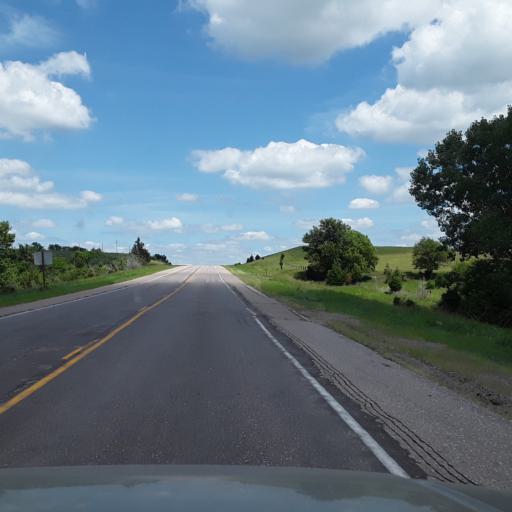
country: US
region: Nebraska
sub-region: Nance County
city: Genoa
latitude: 41.4717
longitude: -97.7047
